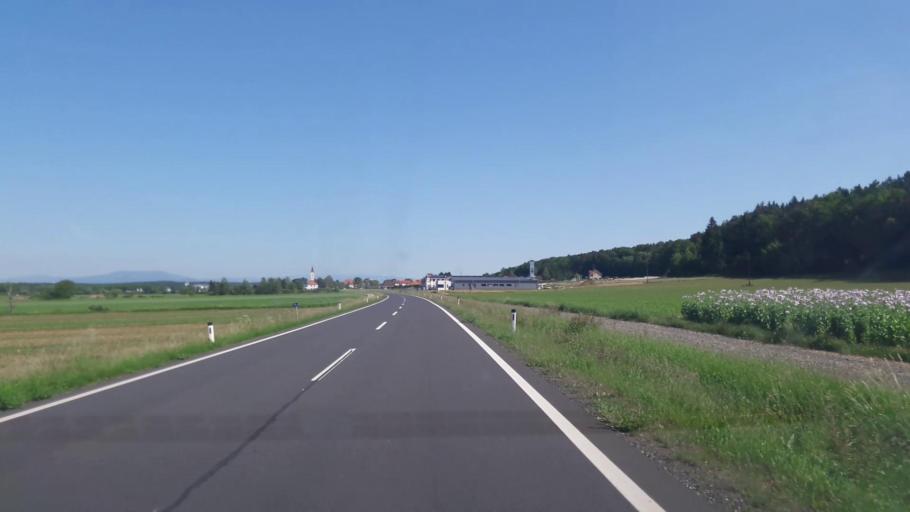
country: AT
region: Burgenland
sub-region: Politischer Bezirk Jennersdorf
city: Deutsch Kaltenbrunn
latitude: 47.0743
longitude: 16.1123
